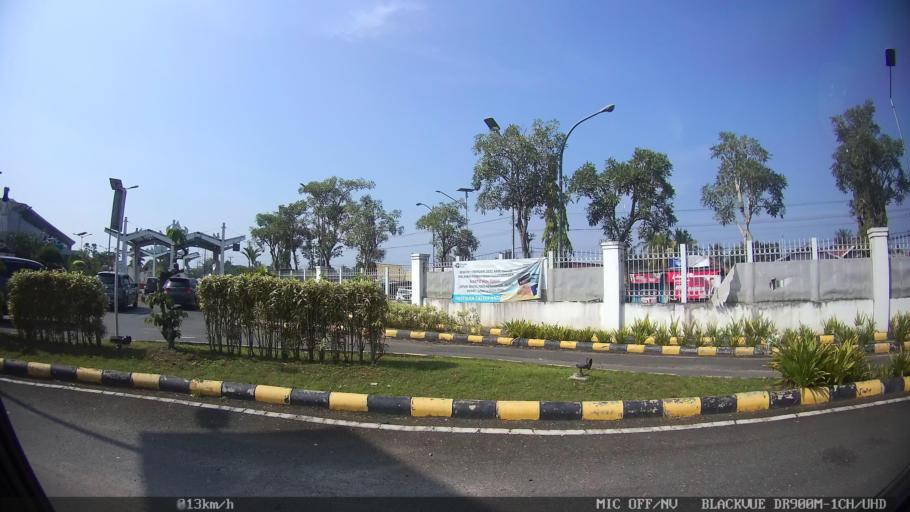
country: ID
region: Lampung
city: Natar
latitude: -5.2426
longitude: 105.1751
